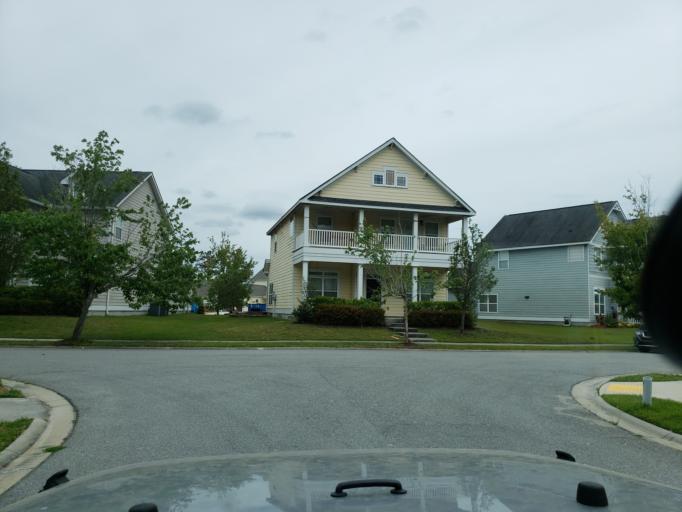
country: US
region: Georgia
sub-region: Chatham County
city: Port Wentworth
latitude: 32.2121
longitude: -81.1792
